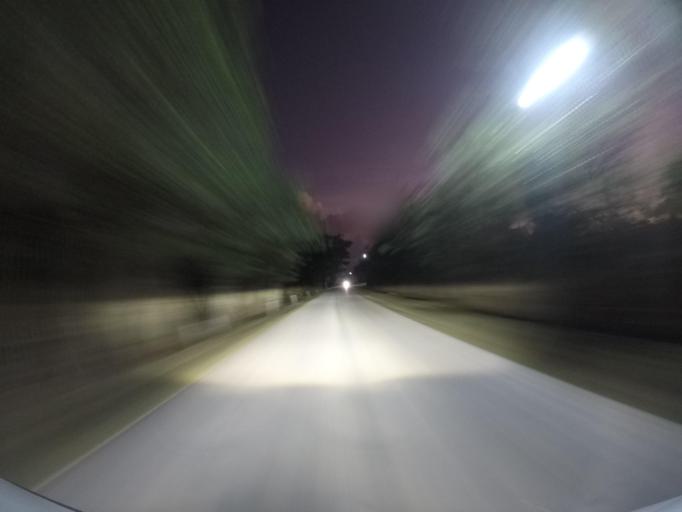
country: TL
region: Lautem
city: Lospalos
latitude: -8.4600
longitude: 126.9987
